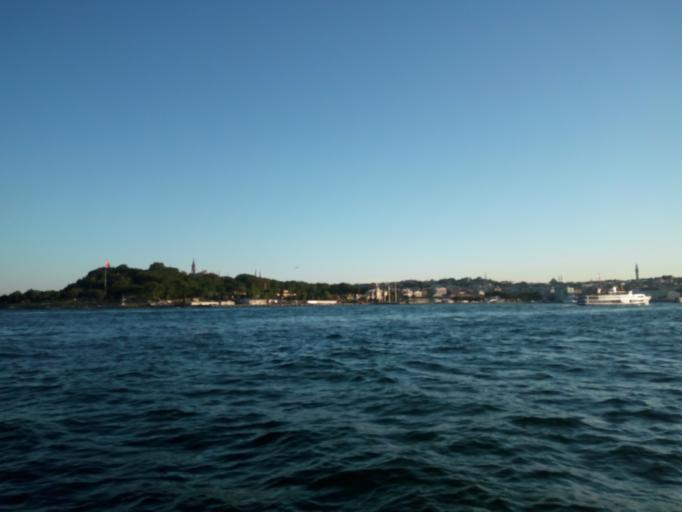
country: TR
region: Istanbul
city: Eminoenue
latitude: 41.0220
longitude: 28.9873
